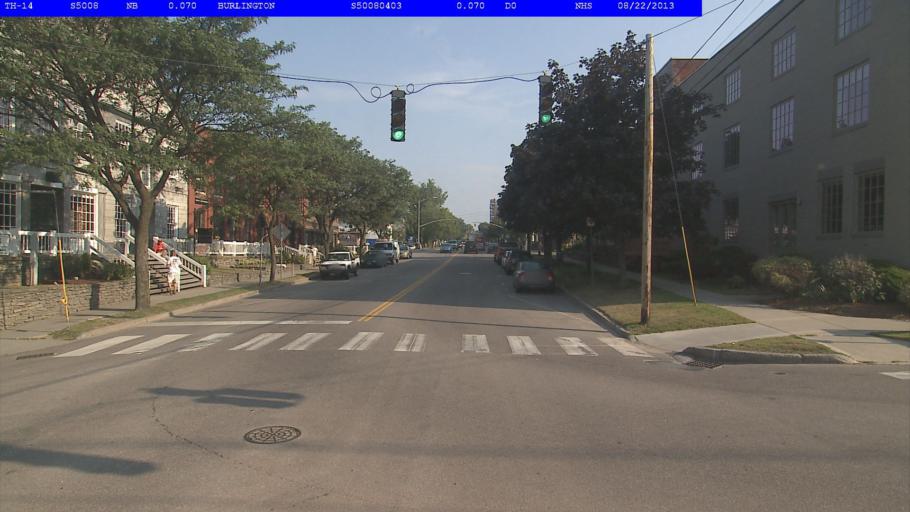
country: US
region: Vermont
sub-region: Chittenden County
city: Burlington
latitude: 44.4734
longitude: -73.2185
